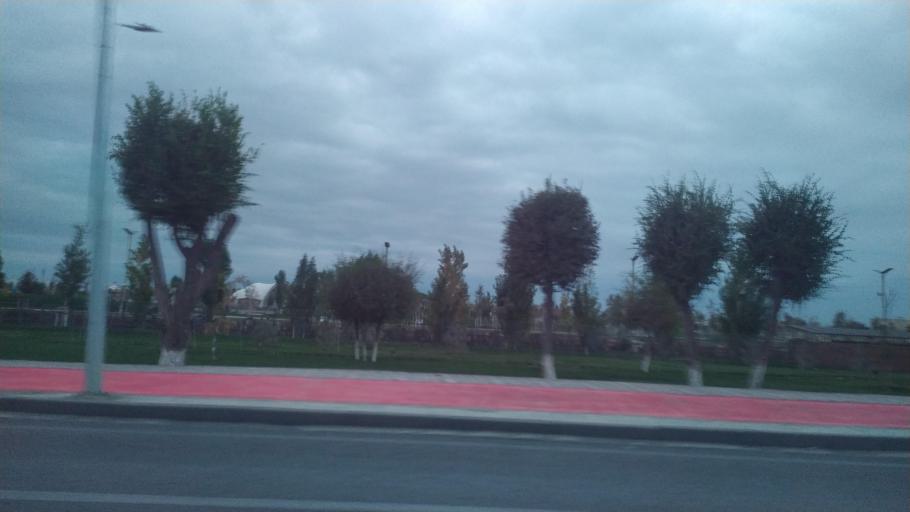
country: KZ
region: Ongtustik Qazaqstan
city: Turkestan
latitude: 43.2762
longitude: 68.3328
